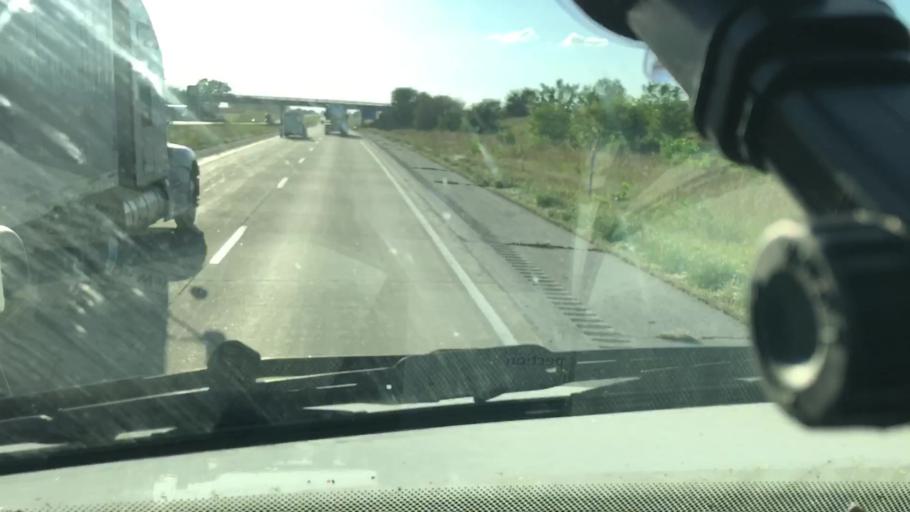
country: US
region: Iowa
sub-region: Pottawattamie County
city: Avoca
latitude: 41.4993
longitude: -95.4773
